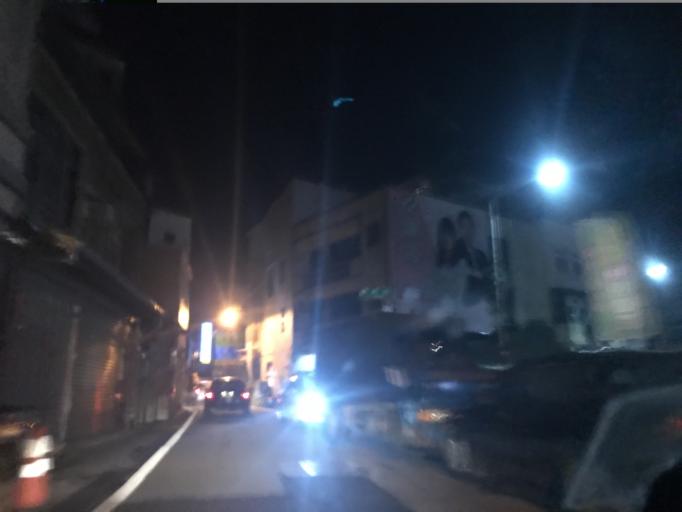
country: TW
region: Taiwan
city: Daxi
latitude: 24.8611
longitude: 121.2121
